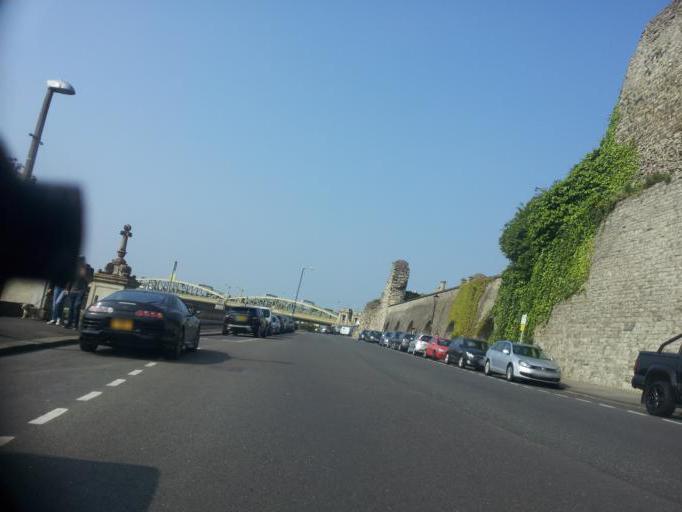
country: GB
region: England
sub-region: Medway
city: Rochester
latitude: 51.3899
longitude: 0.5005
